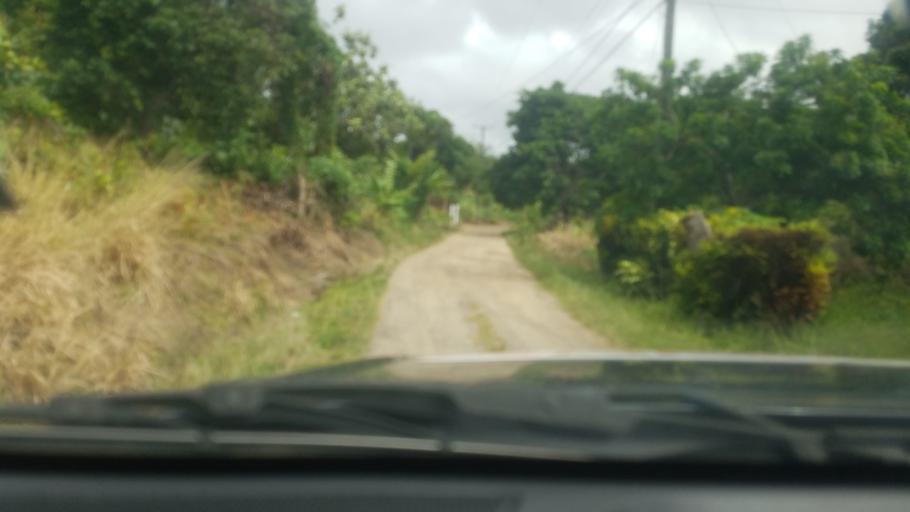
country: LC
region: Micoud Quarter
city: Micoud
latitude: 13.8009
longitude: -60.9335
